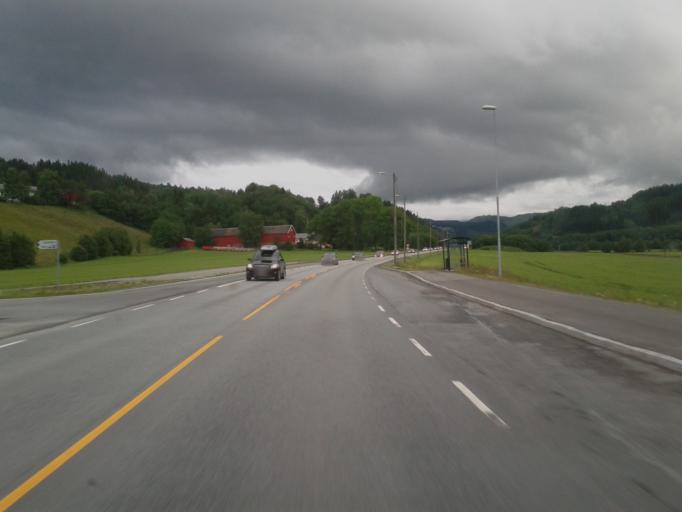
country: NO
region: Sor-Trondelag
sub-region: Melhus
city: Lundamo
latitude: 63.1365
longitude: 10.2531
